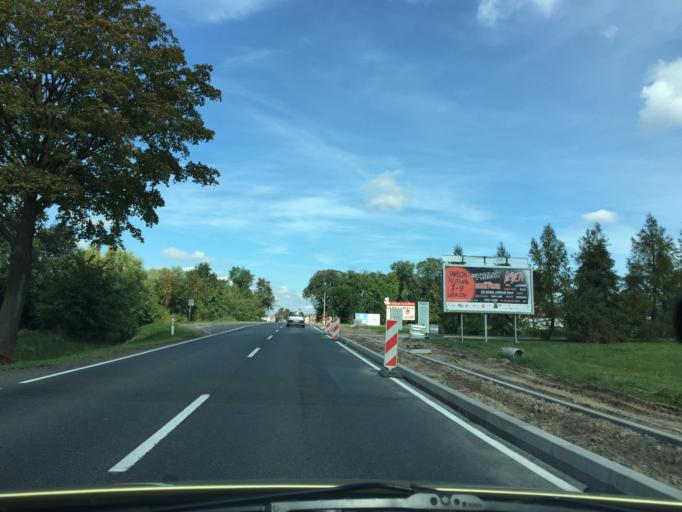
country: PL
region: Greater Poland Voivodeship
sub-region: Kalisz
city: Kalisz
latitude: 51.7939
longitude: 18.0913
